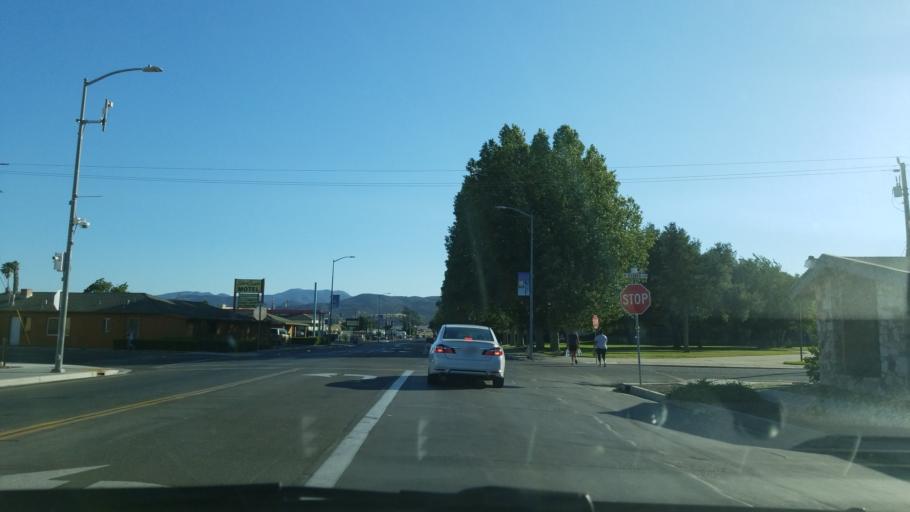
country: US
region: California
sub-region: Monterey County
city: King City
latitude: 36.2098
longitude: -121.1317
